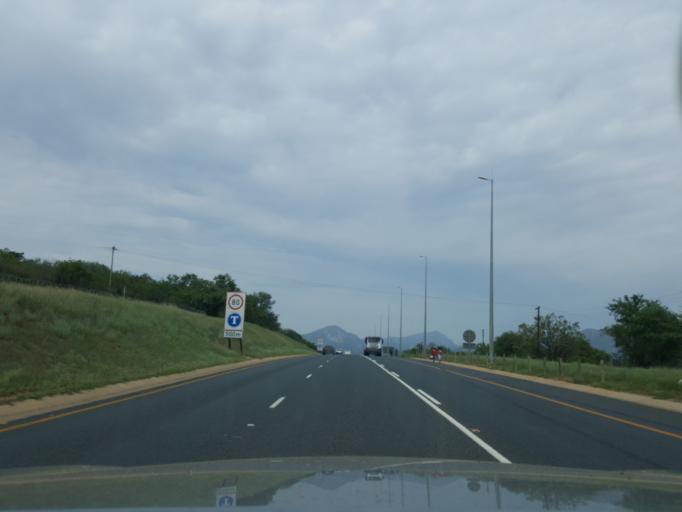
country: SZ
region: Hhohho
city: Ntfonjeni
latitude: -25.5362
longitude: 31.3514
